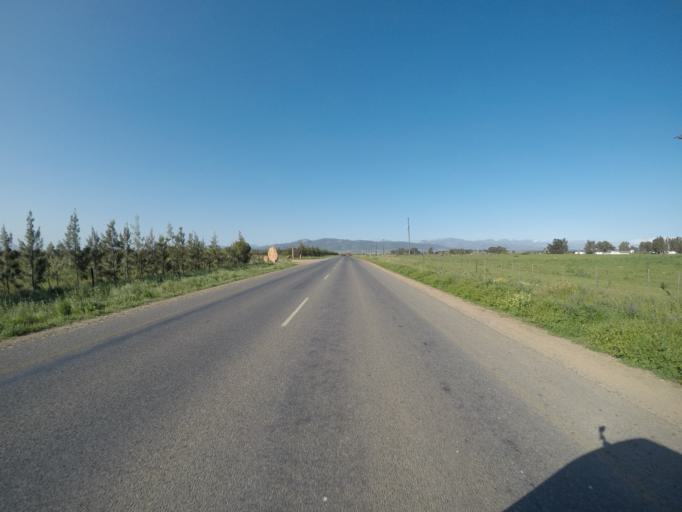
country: ZA
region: Western Cape
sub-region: City of Cape Town
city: Kraaifontein
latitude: -33.7633
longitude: 18.7991
